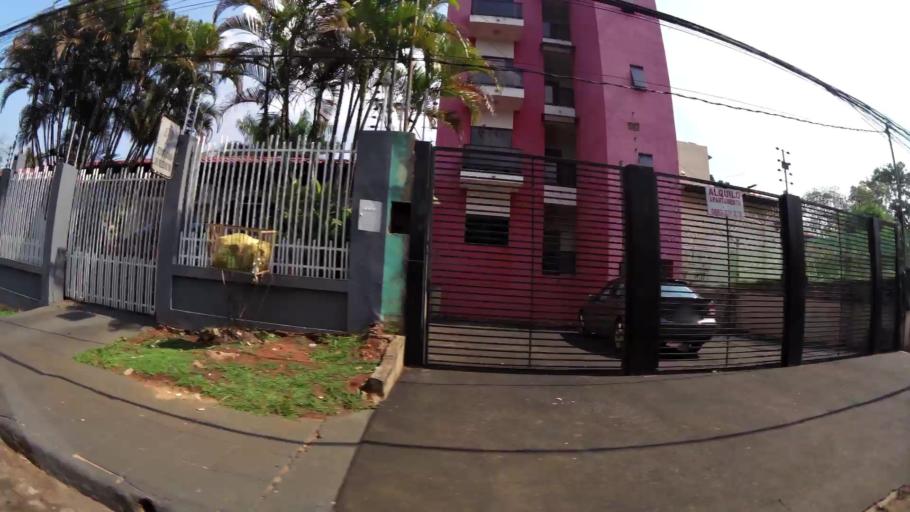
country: PY
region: Alto Parana
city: Ciudad del Este
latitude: -25.5157
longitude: -54.6304
